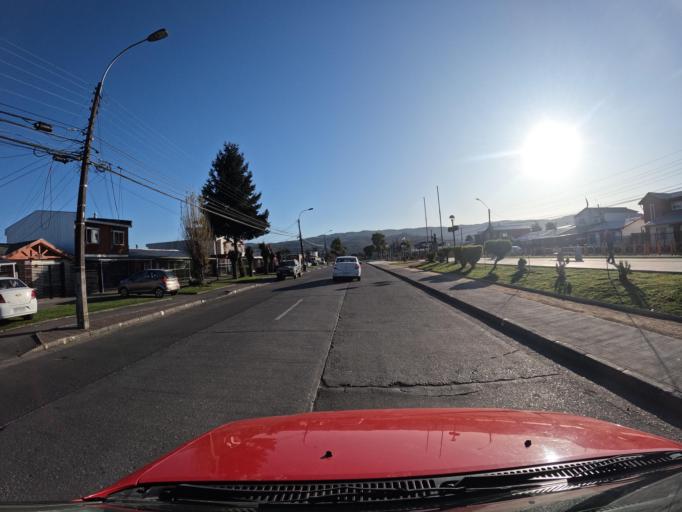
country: CL
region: Biobio
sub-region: Provincia de Concepcion
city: Chiguayante
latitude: -36.9296
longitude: -73.0251
